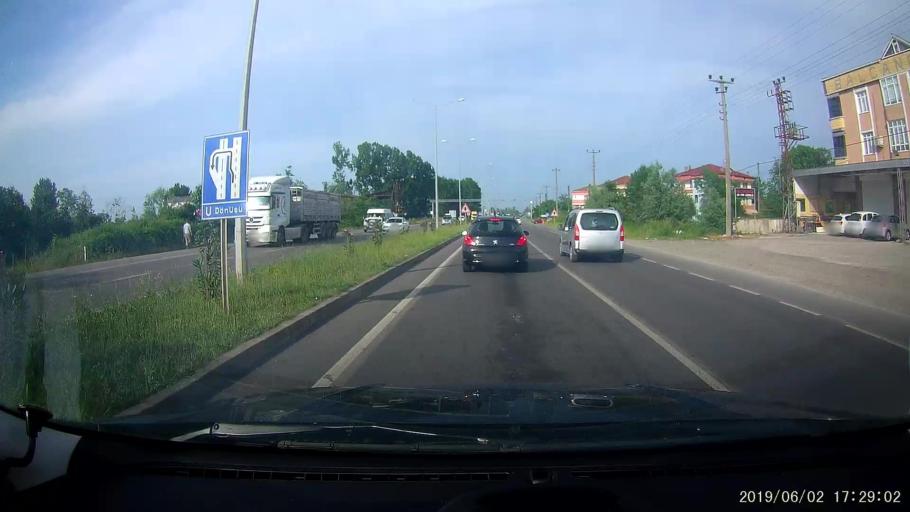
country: TR
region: Samsun
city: Carsamba
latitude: 41.2098
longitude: 36.7529
